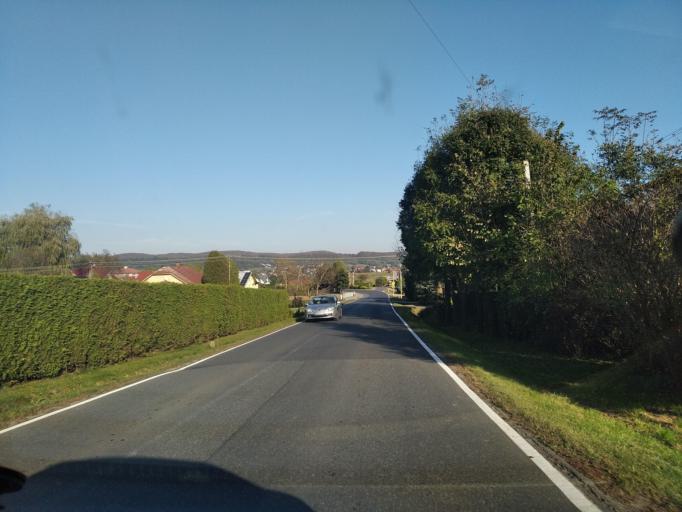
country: PL
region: Subcarpathian Voivodeship
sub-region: Powiat brzozowski
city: Turze Pole
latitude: 49.6710
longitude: 22.0288
